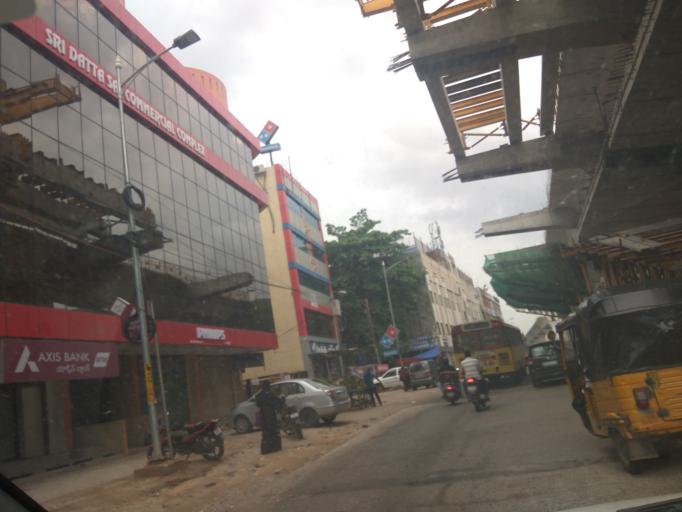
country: IN
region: Telangana
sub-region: Hyderabad
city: Hyderabad
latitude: 17.4082
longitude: 78.4974
